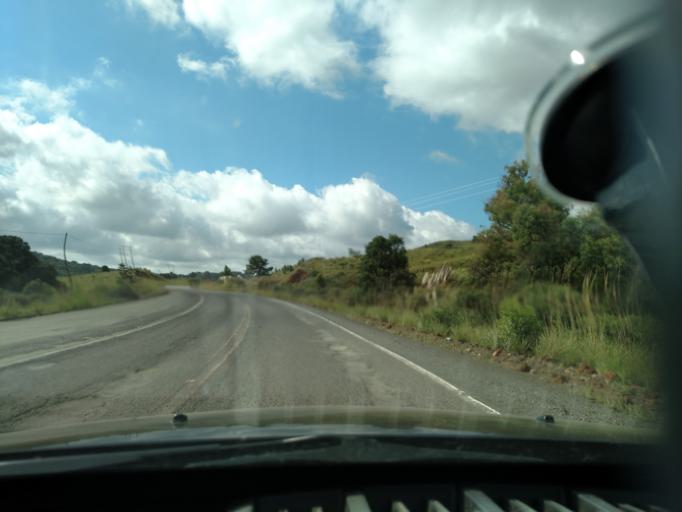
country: BR
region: Santa Catarina
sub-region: Lages
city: Lages
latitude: -27.8766
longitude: -50.1780
